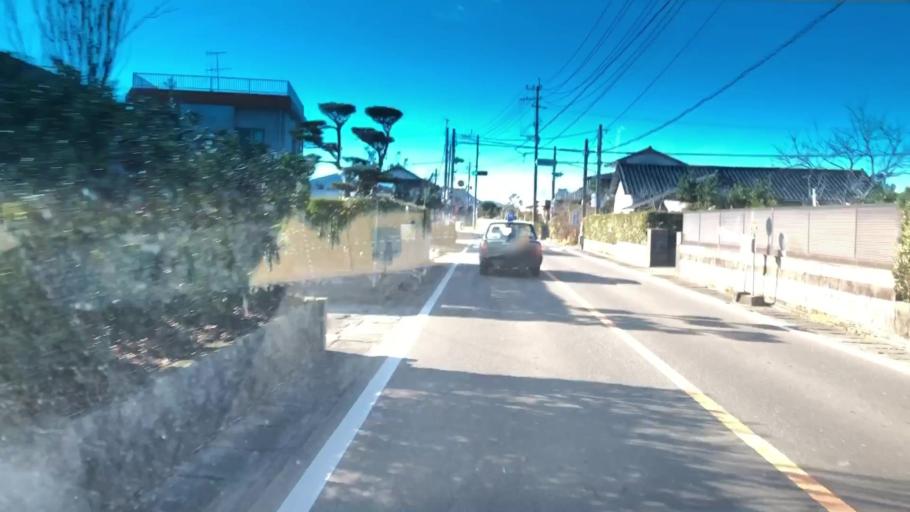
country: JP
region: Kagoshima
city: Satsumasendai
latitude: 31.8239
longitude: 130.2544
